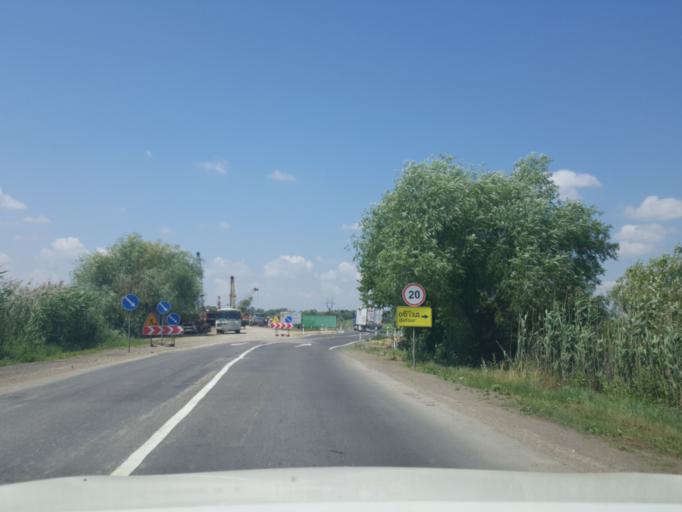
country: UA
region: Odessa
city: Bilyayivka
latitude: 46.4140
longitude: 30.1589
